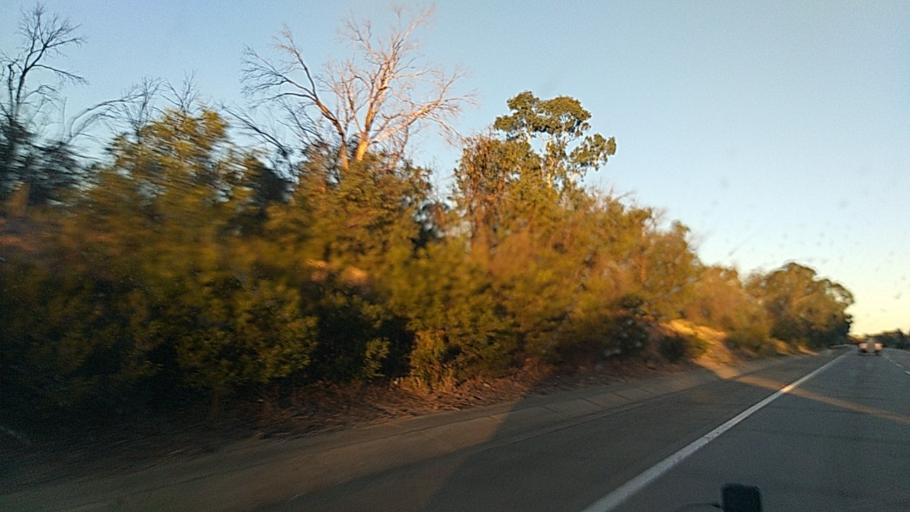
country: AU
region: New South Wales
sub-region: Goulburn Mulwaree
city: Goulburn
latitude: -34.7760
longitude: 149.6976
